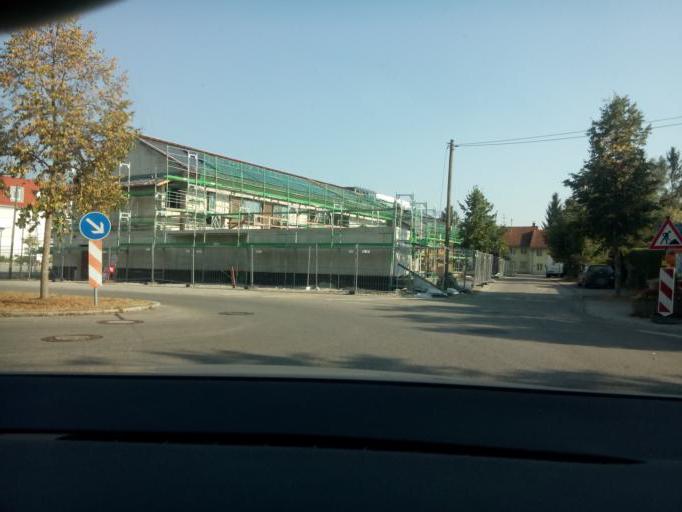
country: DE
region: Bavaria
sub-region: Upper Bavaria
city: Unterhaching
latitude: 48.0831
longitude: 11.6276
